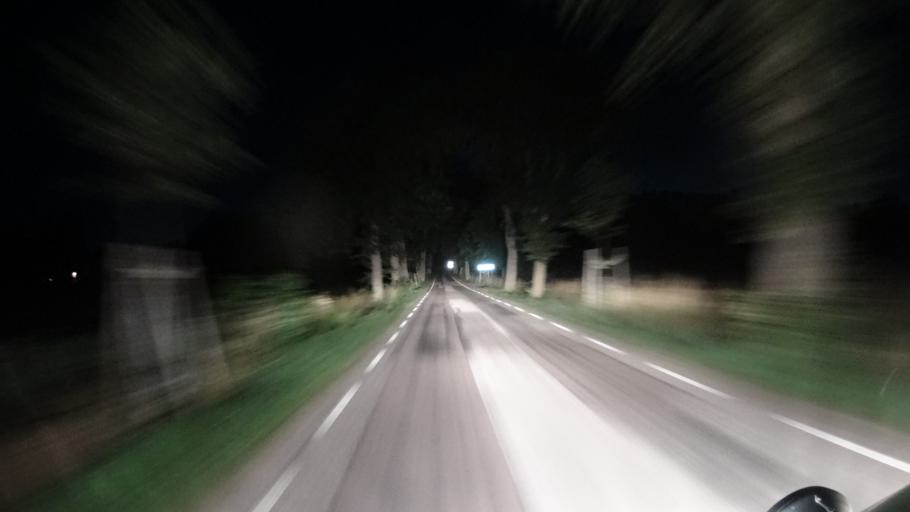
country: SE
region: OEstergoetland
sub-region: Vadstena Kommun
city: Herrestad
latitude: 58.3196
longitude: 14.8420
